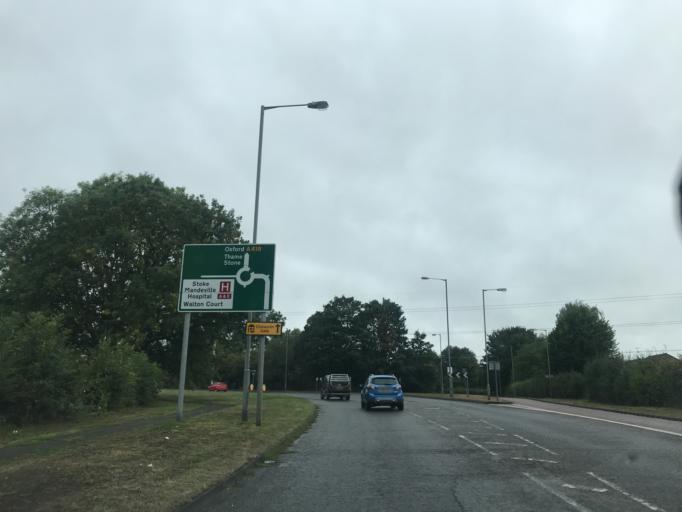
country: GB
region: England
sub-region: Buckinghamshire
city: Aylesbury
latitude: 51.8105
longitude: -0.8300
